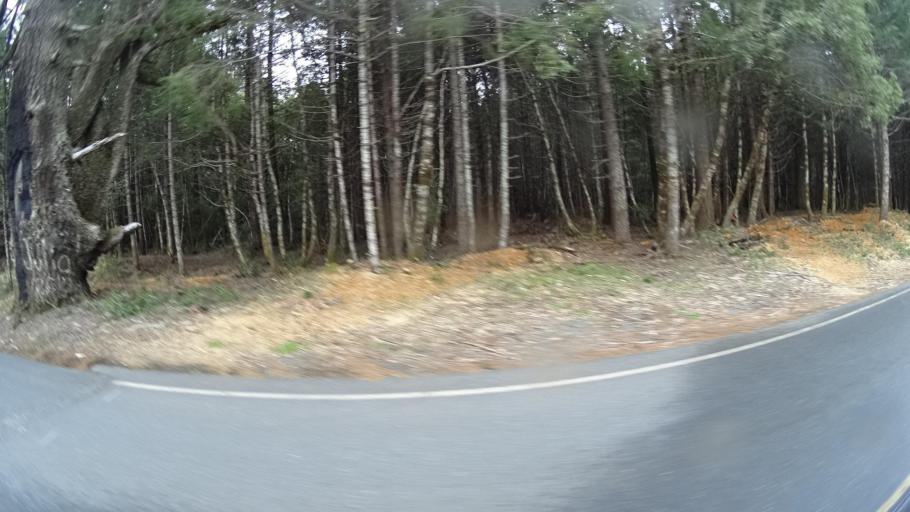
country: US
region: California
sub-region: Humboldt County
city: Willow Creek
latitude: 41.2010
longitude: -123.8032
